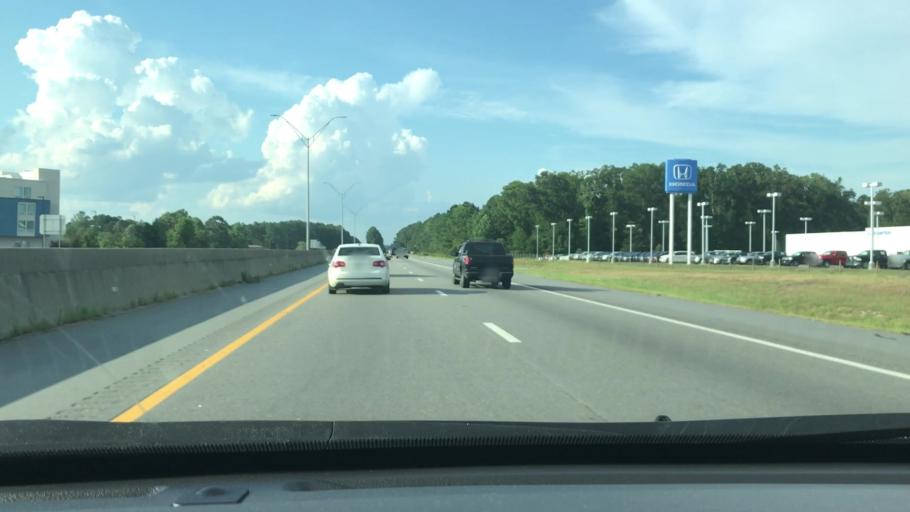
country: US
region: North Carolina
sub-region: Robeson County
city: Lumberton
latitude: 34.6718
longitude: -79.0054
